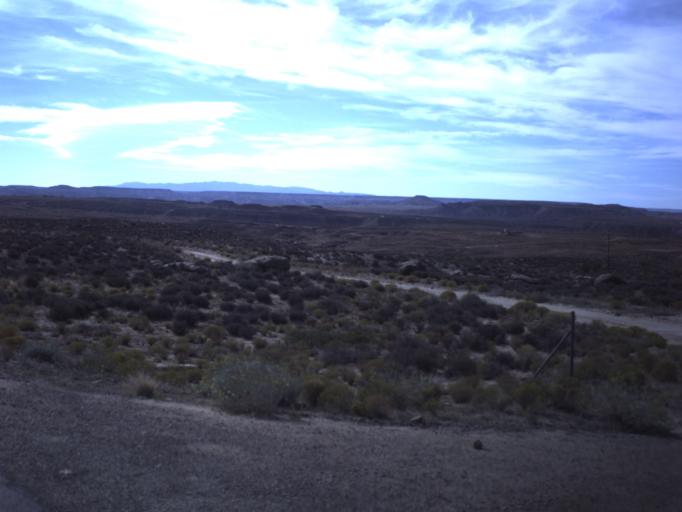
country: US
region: Utah
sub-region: San Juan County
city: Blanding
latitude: 37.3176
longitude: -109.3079
